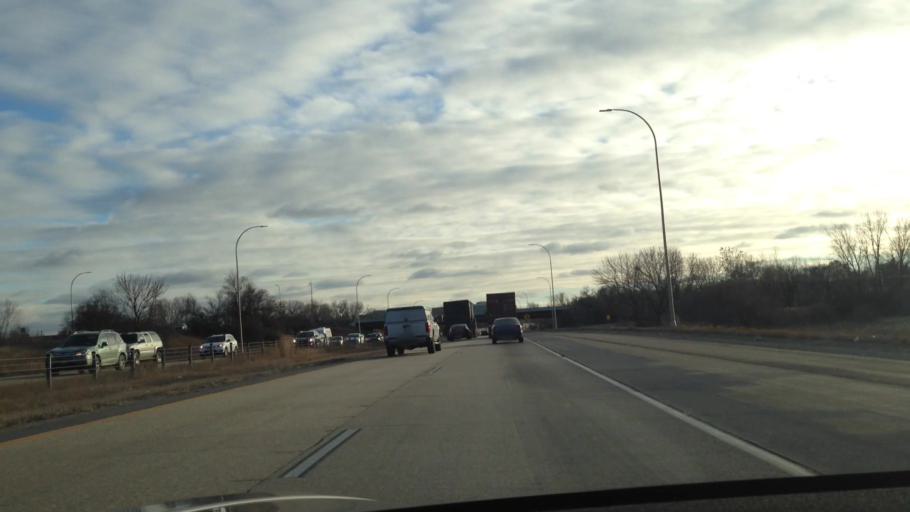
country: US
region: Minnesota
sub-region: Hennepin County
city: Minnetonka Mills
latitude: 44.9371
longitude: -93.3962
